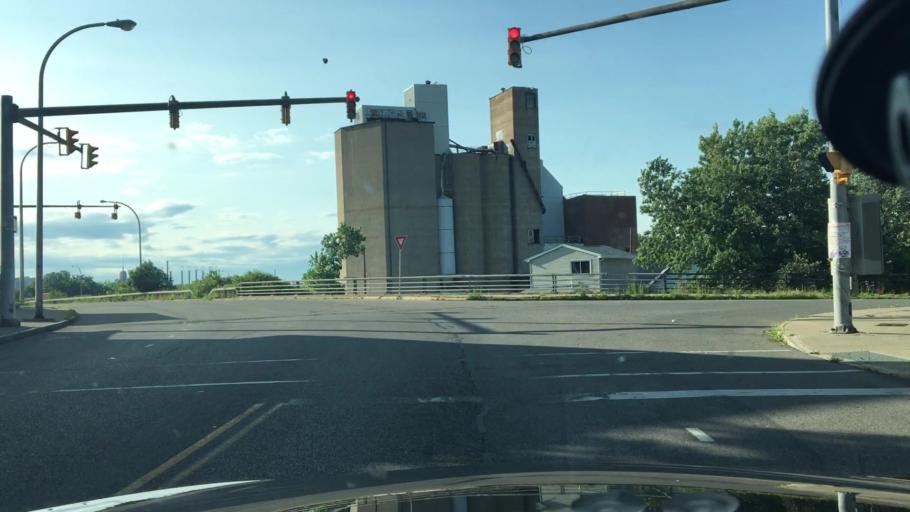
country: US
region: New York
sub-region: Erie County
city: Buffalo
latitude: 42.8685
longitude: -78.8509
